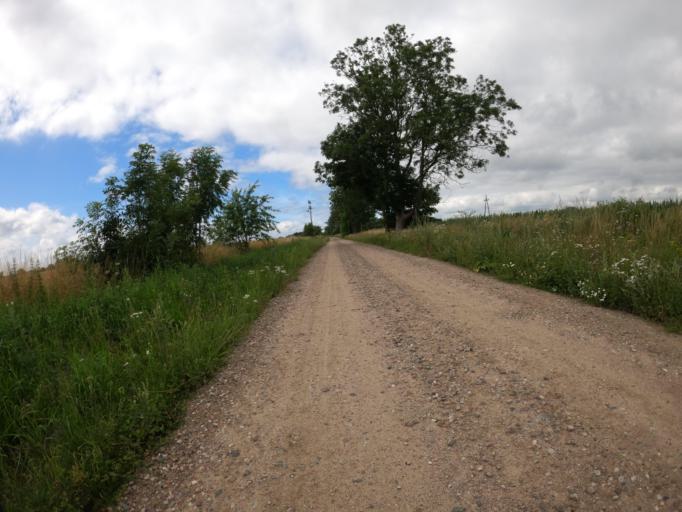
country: PL
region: West Pomeranian Voivodeship
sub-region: Powiat bialogardzki
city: Tychowo
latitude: 53.9978
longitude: 16.3763
